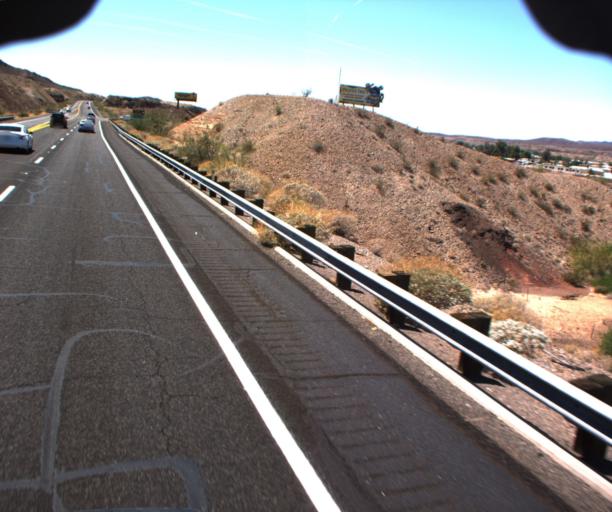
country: US
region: Arizona
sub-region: La Paz County
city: Cienega Springs
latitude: 34.2178
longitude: -114.1933
